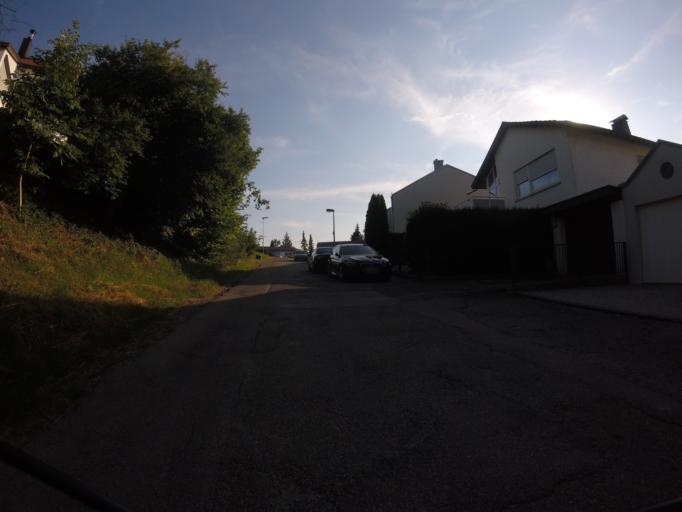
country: DE
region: Baden-Wuerttemberg
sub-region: Regierungsbezirk Stuttgart
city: Asperg
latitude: 48.9099
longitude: 9.1333
